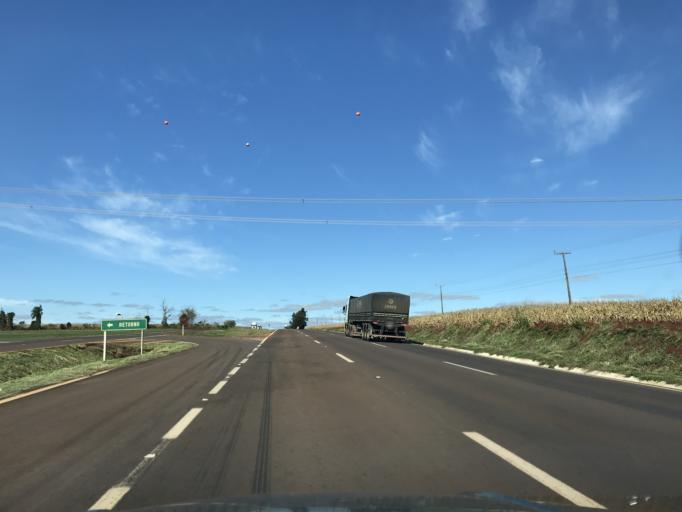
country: BR
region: Parana
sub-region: Cascavel
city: Cascavel
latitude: -24.9048
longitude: -53.5169
